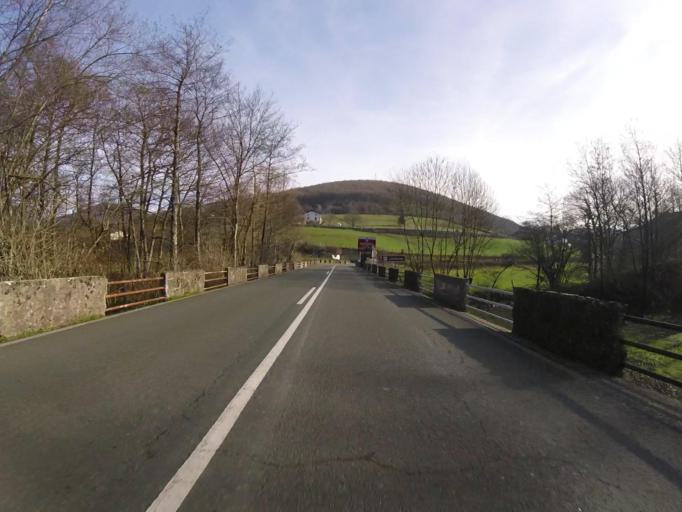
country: ES
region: Navarre
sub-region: Provincia de Navarra
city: Areso
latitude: 43.0977
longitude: -1.9479
